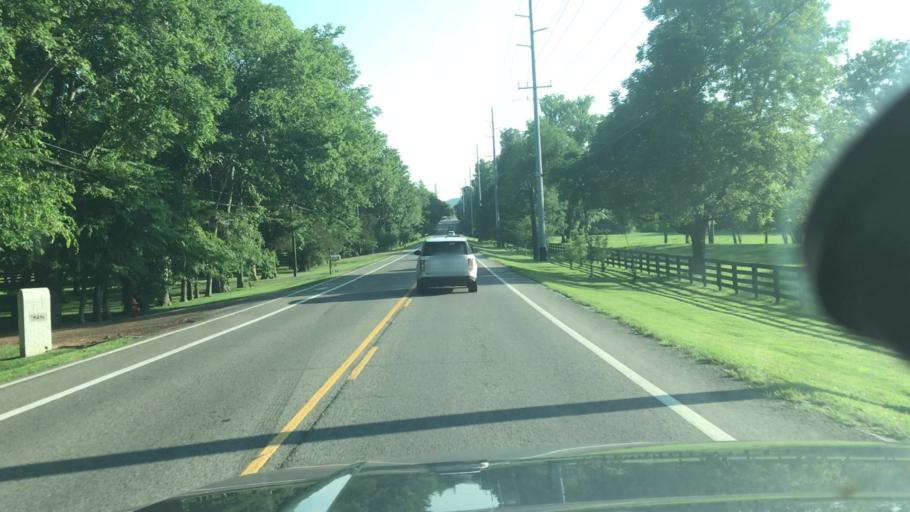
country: US
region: Tennessee
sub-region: Davidson County
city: Forest Hills
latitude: 36.0552
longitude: -86.8559
